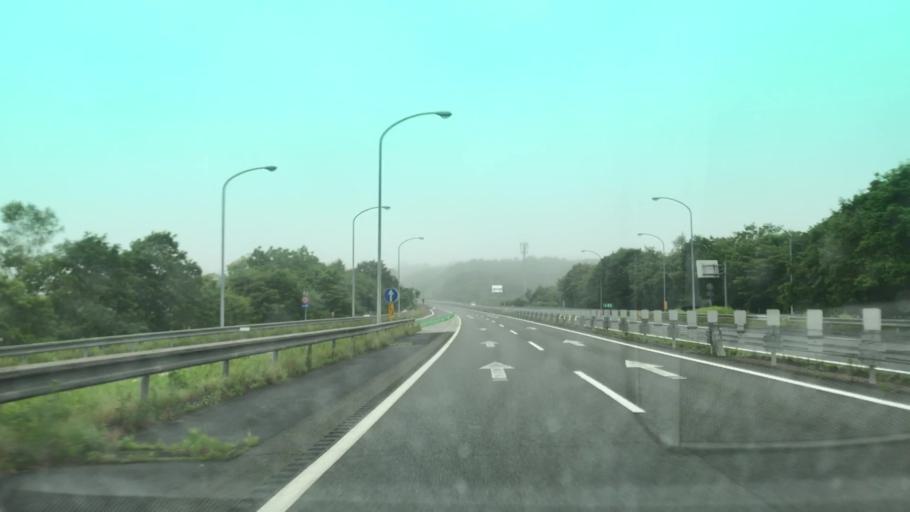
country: JP
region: Hokkaido
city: Tomakomai
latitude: 42.6324
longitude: 141.4893
